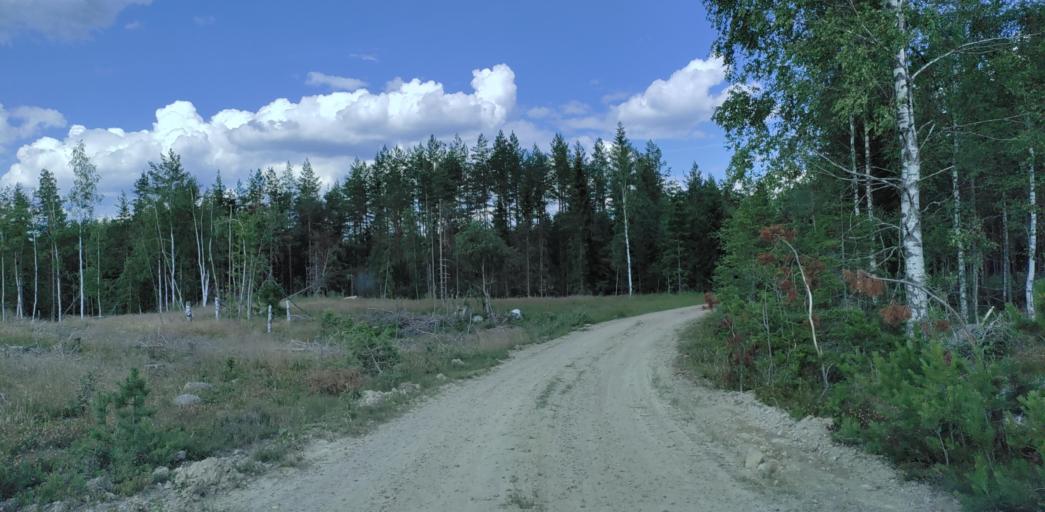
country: SE
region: Vaermland
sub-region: Hagfors Kommun
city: Ekshaerad
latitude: 60.0769
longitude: 13.3455
